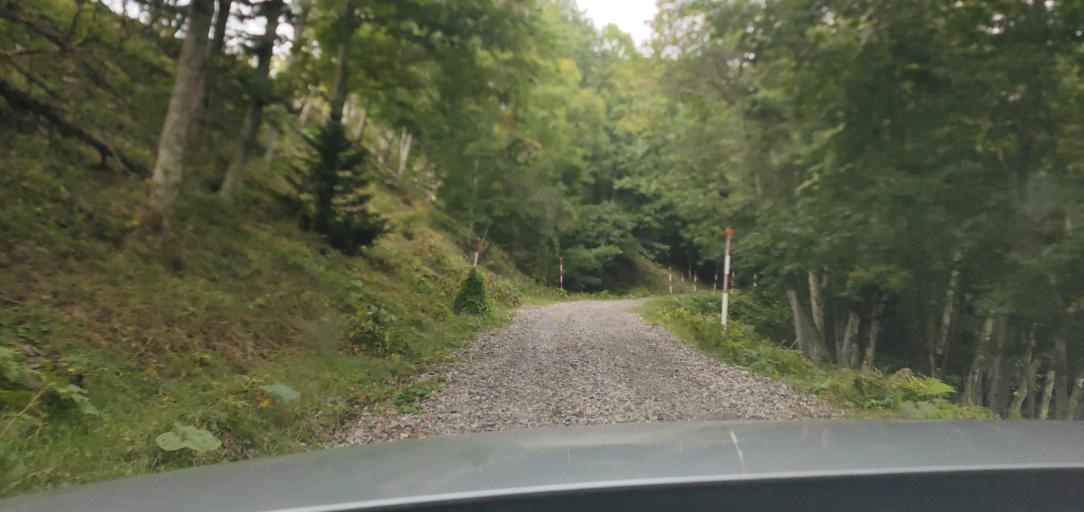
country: JP
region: Hokkaido
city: Kitami
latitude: 43.3666
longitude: 143.9339
